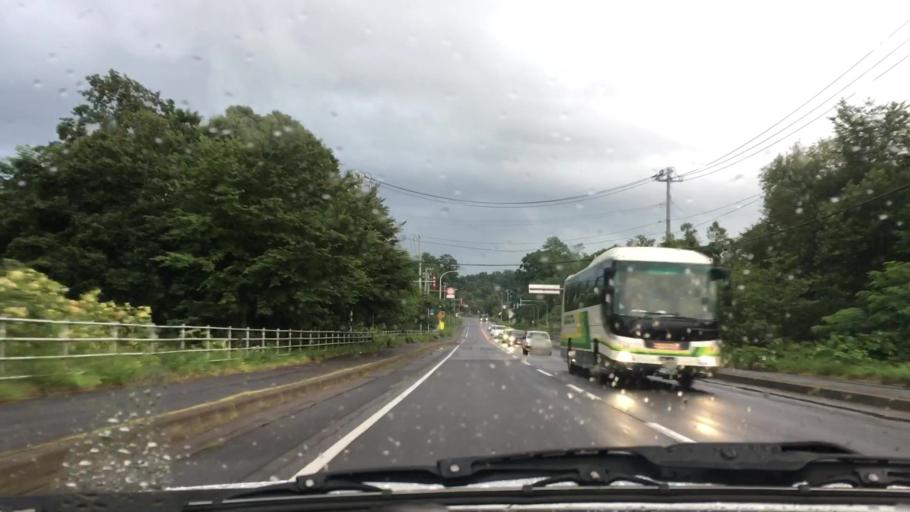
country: JP
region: Hokkaido
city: Nanae
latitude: 42.0858
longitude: 140.5843
